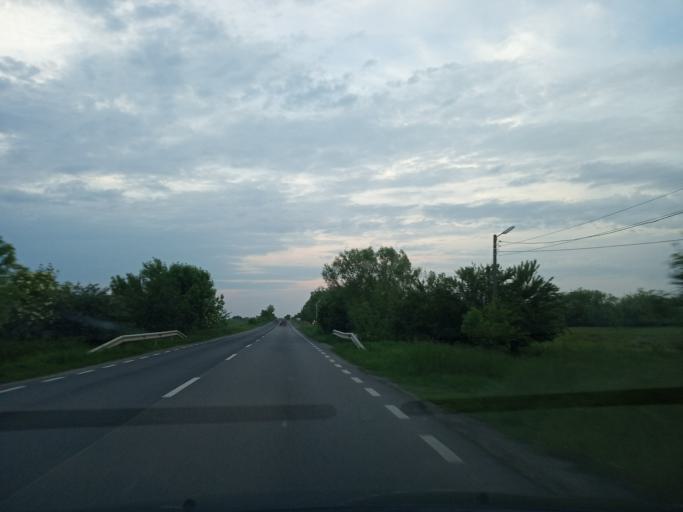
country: RO
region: Timis
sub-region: Comuna Voiteg
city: Voiteg
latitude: 45.4741
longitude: 21.2342
